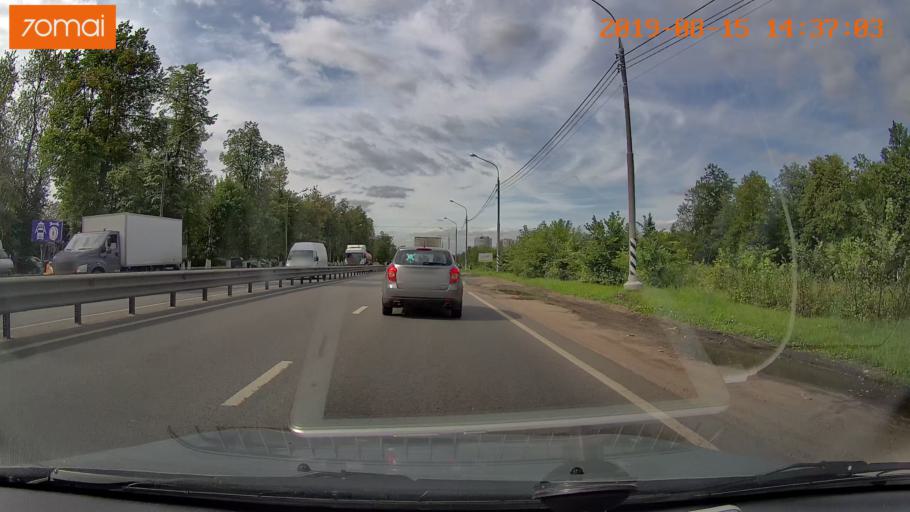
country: RU
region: Moskovskaya
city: Tomilino
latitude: 55.6505
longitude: 37.9302
